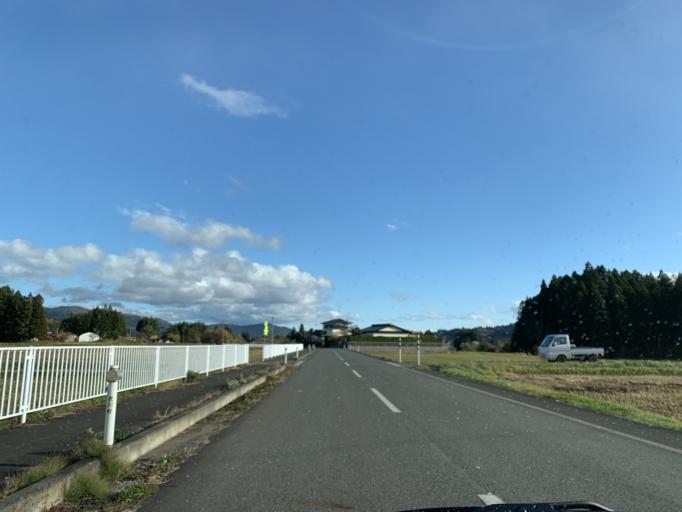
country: JP
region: Iwate
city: Ichinoseki
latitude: 39.0221
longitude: 141.0810
